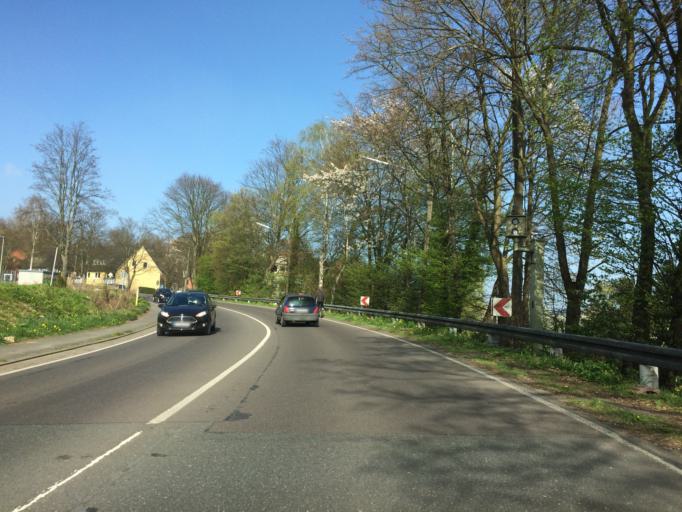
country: DE
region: North Rhine-Westphalia
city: Hattingen
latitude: 51.4102
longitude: 7.1768
